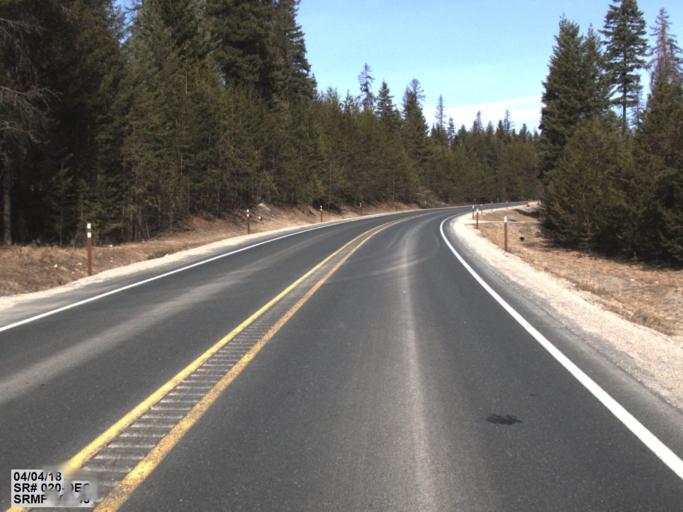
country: US
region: Washington
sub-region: Stevens County
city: Colville
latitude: 48.5140
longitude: -117.6829
